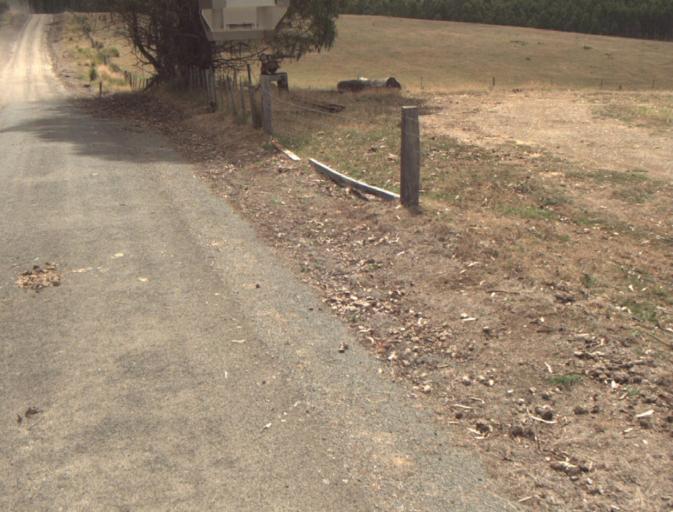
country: AU
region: Tasmania
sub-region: Dorset
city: Scottsdale
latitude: -41.4149
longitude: 147.5251
